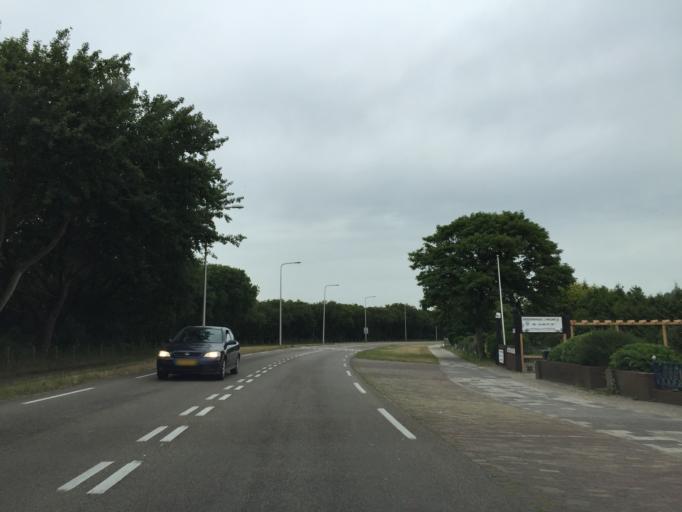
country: NL
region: South Holland
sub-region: Gemeente Westland
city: Poeldijk
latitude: 52.0431
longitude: 4.1996
